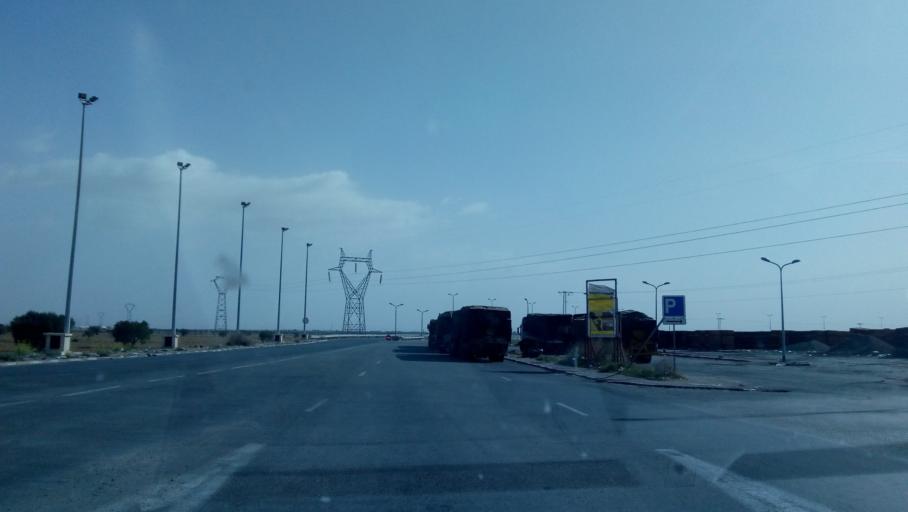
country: TN
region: Qabis
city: Gabes
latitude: 33.8841
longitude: 10.0005
